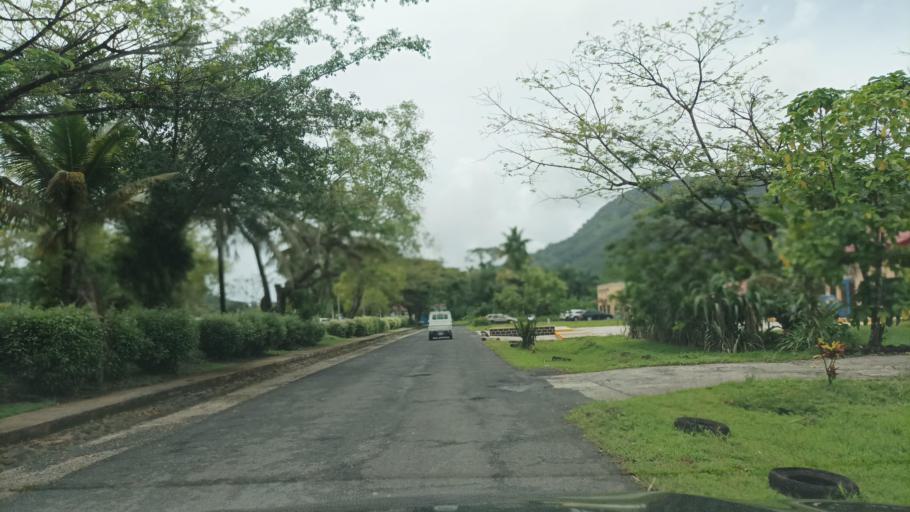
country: FM
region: Pohnpei
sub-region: Sokehs Municipality
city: Palikir - National Government Center
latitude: 6.9234
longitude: 158.1587
